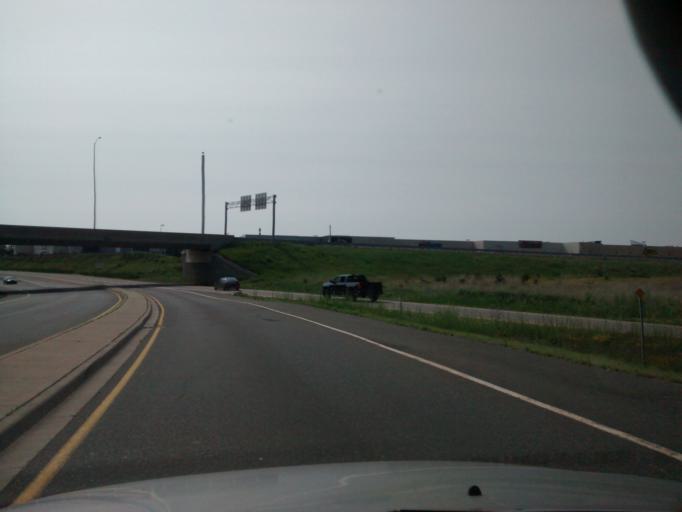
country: CA
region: Ontario
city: Hamilton
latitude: 43.1971
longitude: -79.8132
